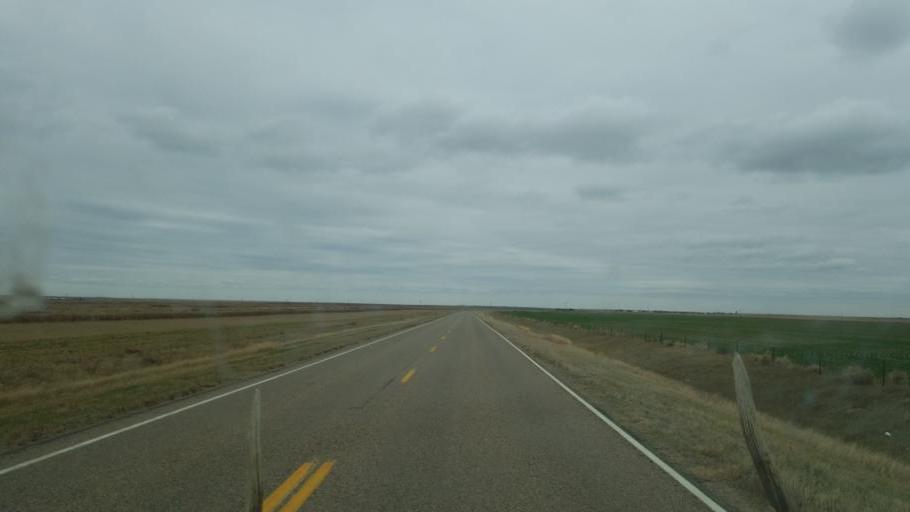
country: US
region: Colorado
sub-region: Cheyenne County
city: Cheyenne Wells
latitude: 38.8512
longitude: -102.2307
